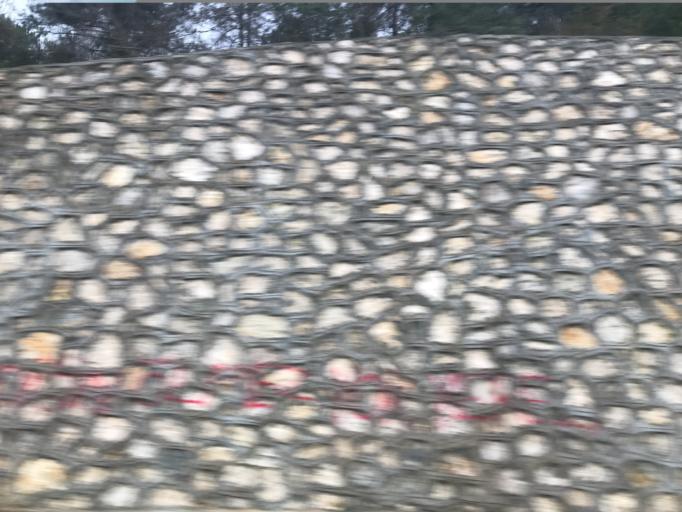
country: TR
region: Bartin
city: Amasra
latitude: 41.7339
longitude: 32.3726
